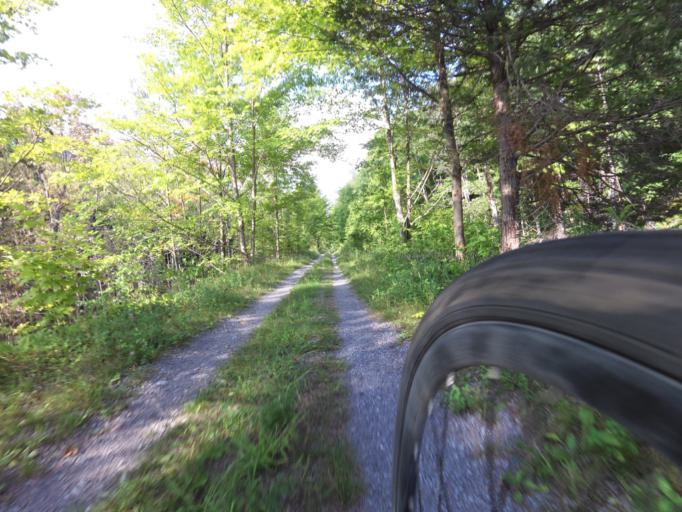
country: CA
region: Ontario
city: Kingston
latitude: 44.4500
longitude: -76.5243
